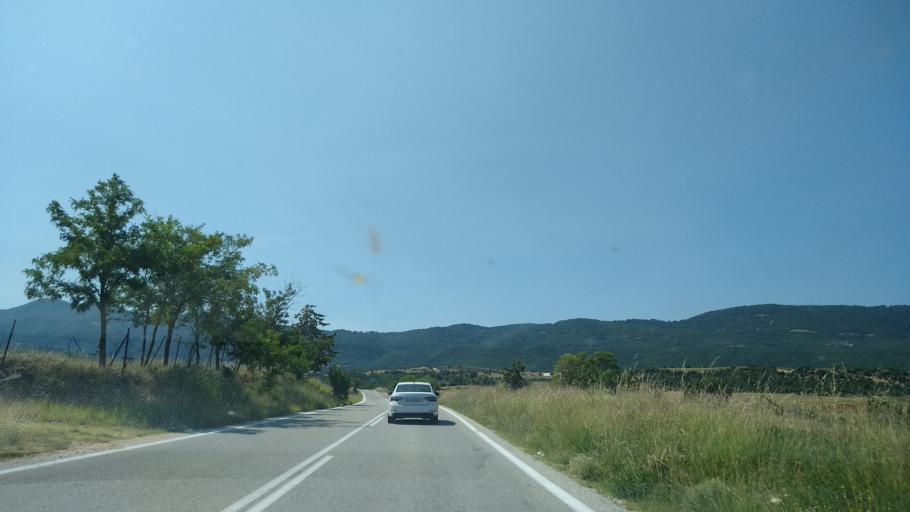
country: GR
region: Central Macedonia
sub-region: Nomos Thessalonikis
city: Nea Apollonia
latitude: 40.5118
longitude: 23.4729
